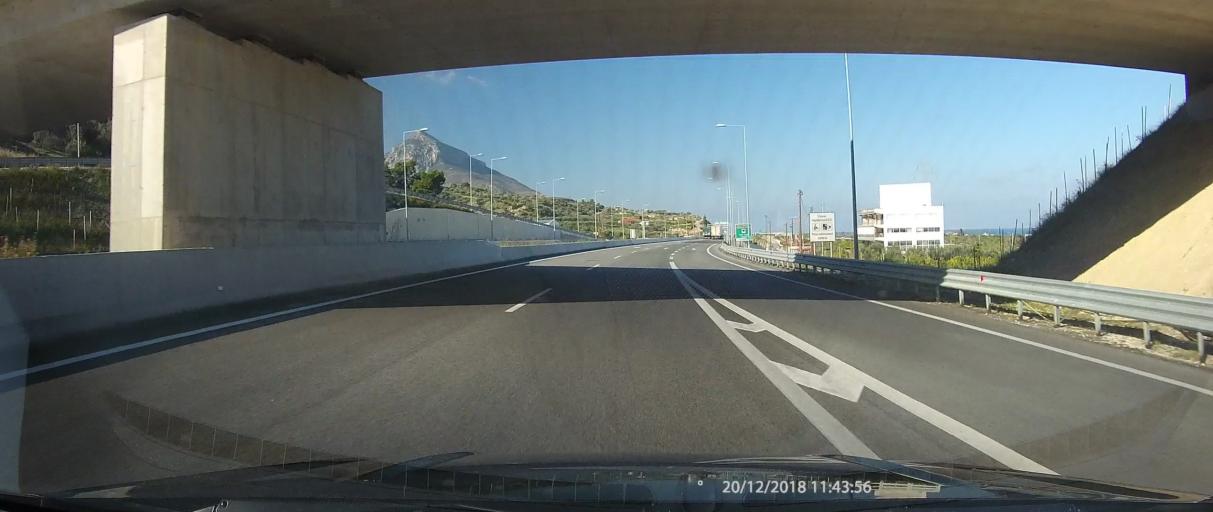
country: GR
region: Peloponnese
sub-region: Nomos Korinthias
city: Xylokastro
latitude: 38.0736
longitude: 22.6136
